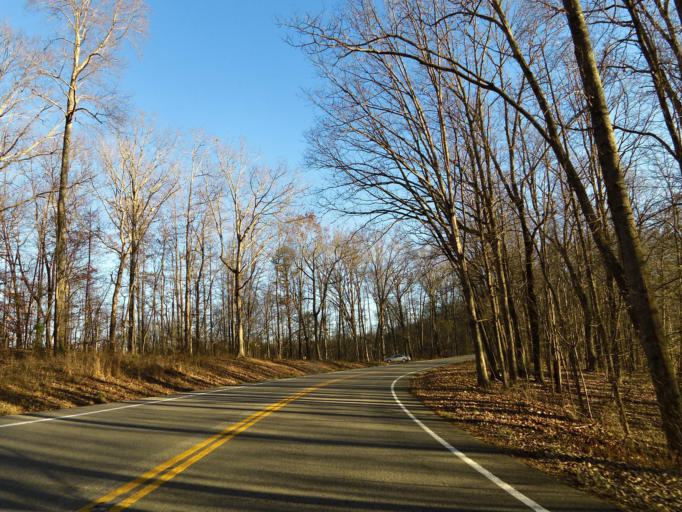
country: US
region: Tennessee
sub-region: Campbell County
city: Pine Crest
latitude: 36.2310
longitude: -84.1051
